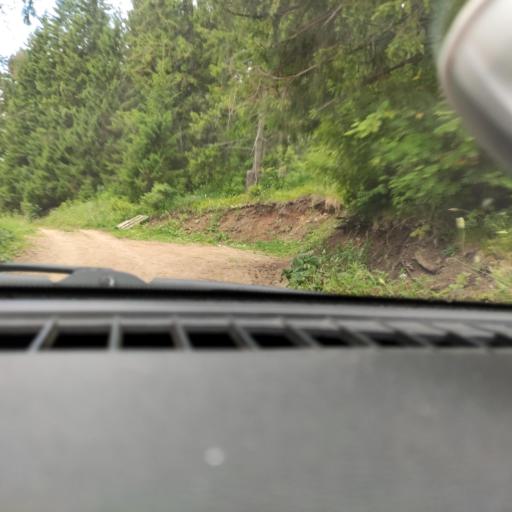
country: RU
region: Perm
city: Polazna
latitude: 58.3495
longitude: 56.2447
